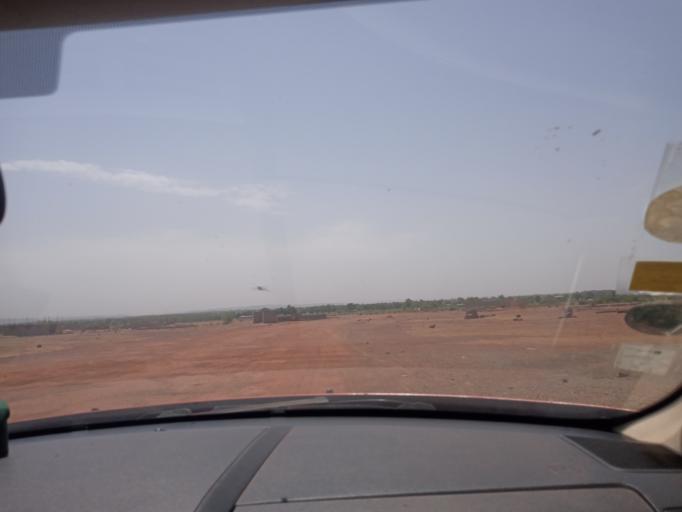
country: ML
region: Bamako
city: Bamako
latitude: 12.5195
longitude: -7.7924
